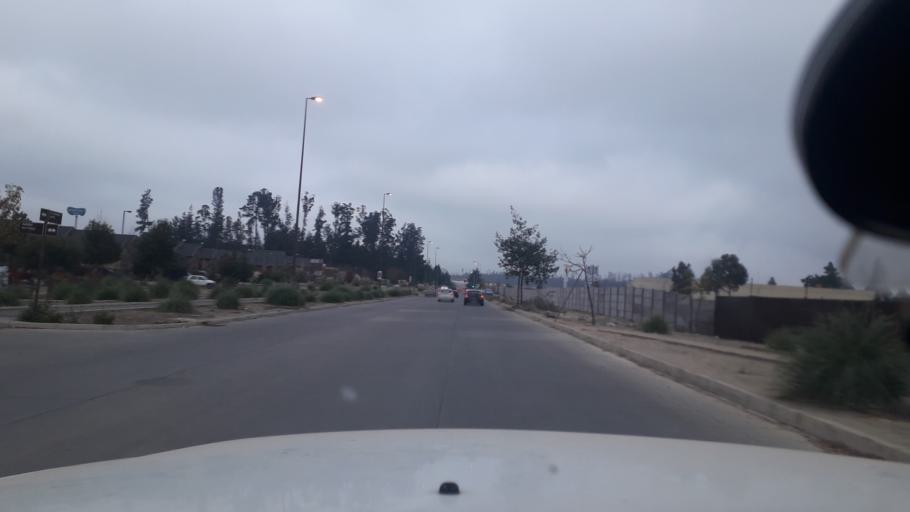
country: CL
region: Valparaiso
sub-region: Provincia de Valparaiso
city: Vina del Mar
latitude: -33.1286
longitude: -71.5663
